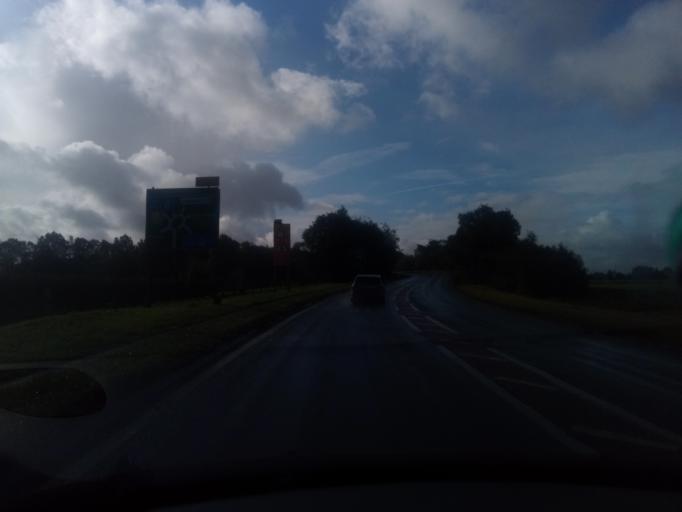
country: GB
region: England
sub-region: Cumbria
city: Carlisle
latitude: 54.9334
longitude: -2.9456
